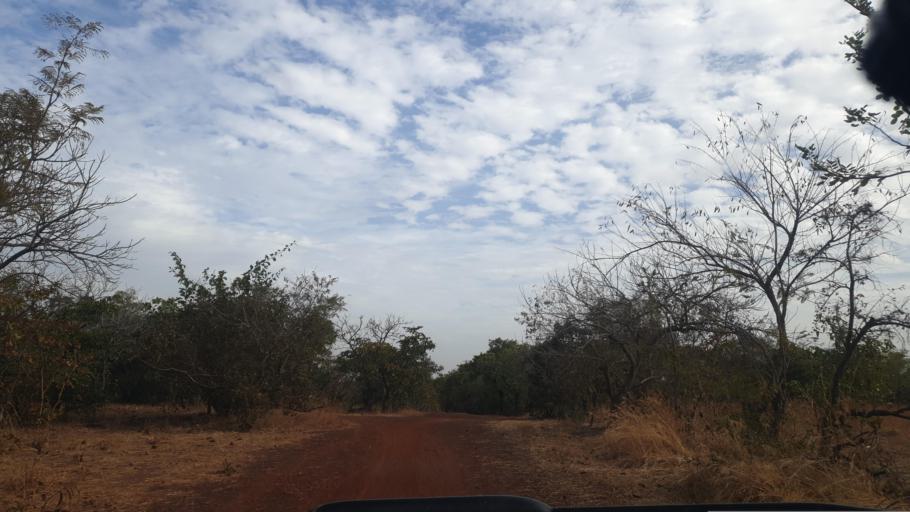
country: ML
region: Sikasso
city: Yanfolila
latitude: 11.3996
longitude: -8.0165
